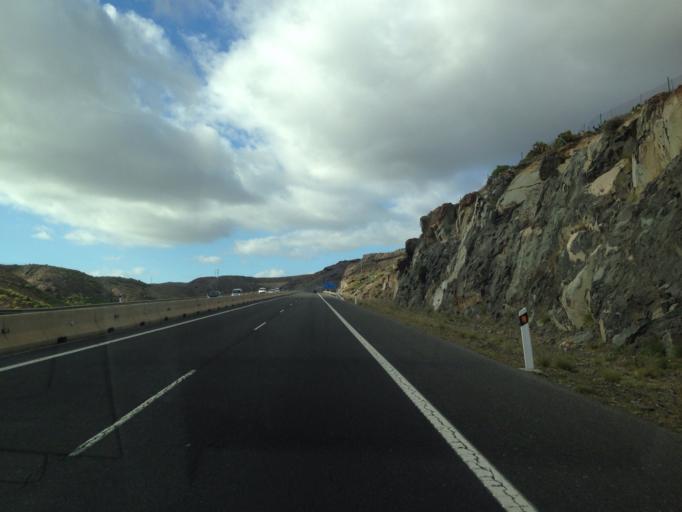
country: ES
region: Canary Islands
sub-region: Provincia de Las Palmas
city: Maspalomas
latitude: 27.7650
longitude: -15.6283
